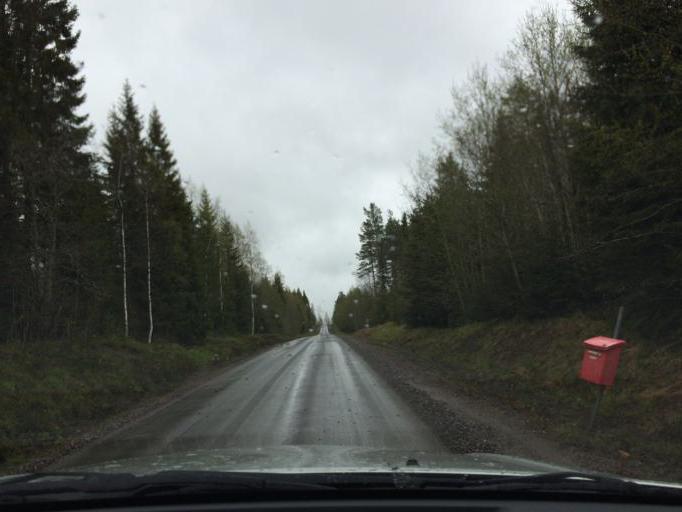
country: SE
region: Dalarna
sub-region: Ludvika Kommun
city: Abborrberget
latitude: 60.0391
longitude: 14.6835
